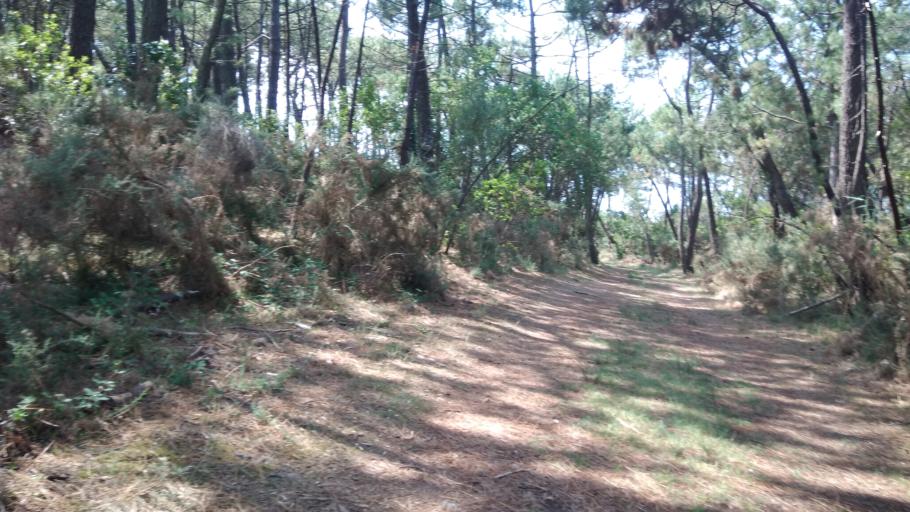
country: FR
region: Aquitaine
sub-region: Departement des Landes
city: Mimizan
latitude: 44.1973
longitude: -1.2963
